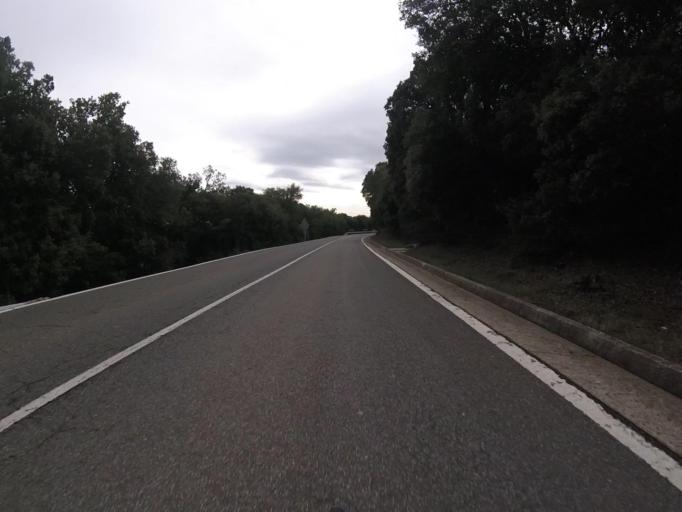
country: ES
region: Navarre
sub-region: Provincia de Navarra
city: Lezaun
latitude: 42.7499
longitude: -2.0136
